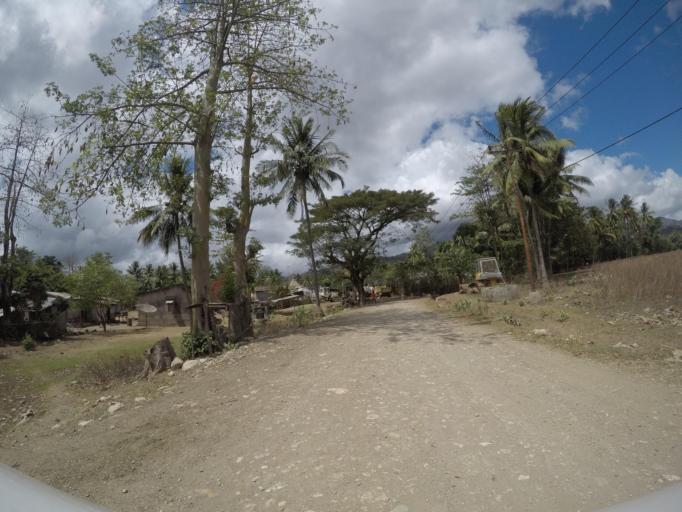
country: TL
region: Lautem
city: Lospalos
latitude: -8.5094
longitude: 126.8325
